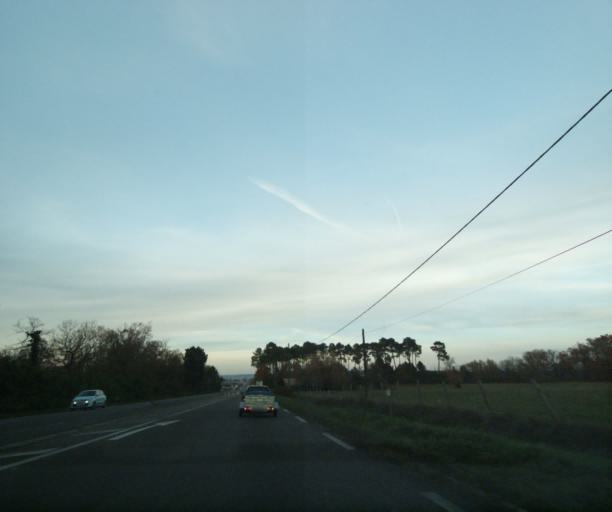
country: FR
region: Aquitaine
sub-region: Departement de la Gironde
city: Langon
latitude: 44.5127
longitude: -0.2391
